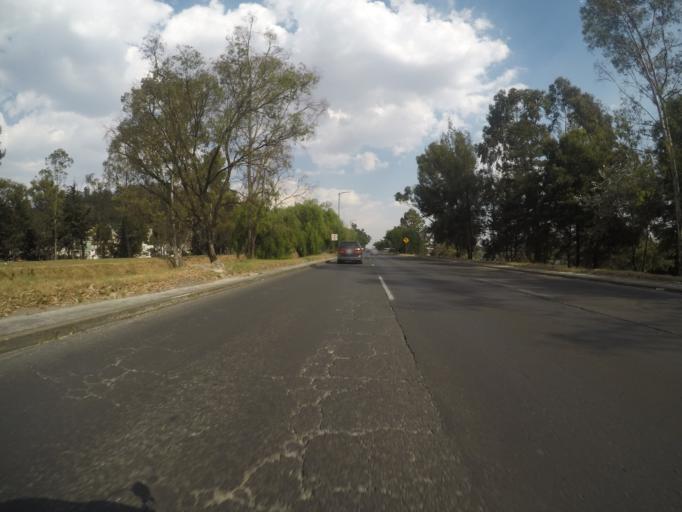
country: MX
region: Morelos
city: Metepec
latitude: 19.2478
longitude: -99.6097
